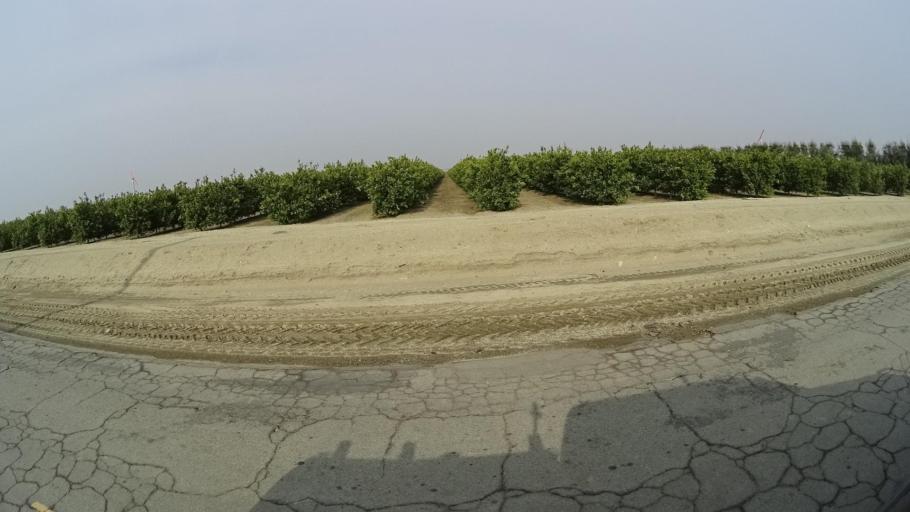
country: US
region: California
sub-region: Kern County
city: Arvin
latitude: 35.1509
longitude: -118.8339
